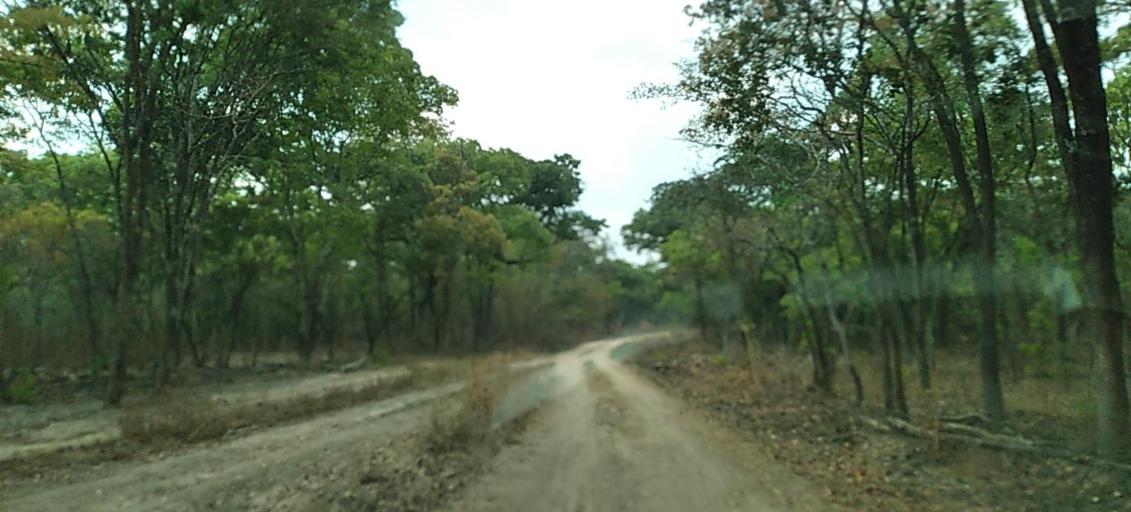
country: ZM
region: Copperbelt
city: Chingola
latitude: -12.7584
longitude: 27.7067
